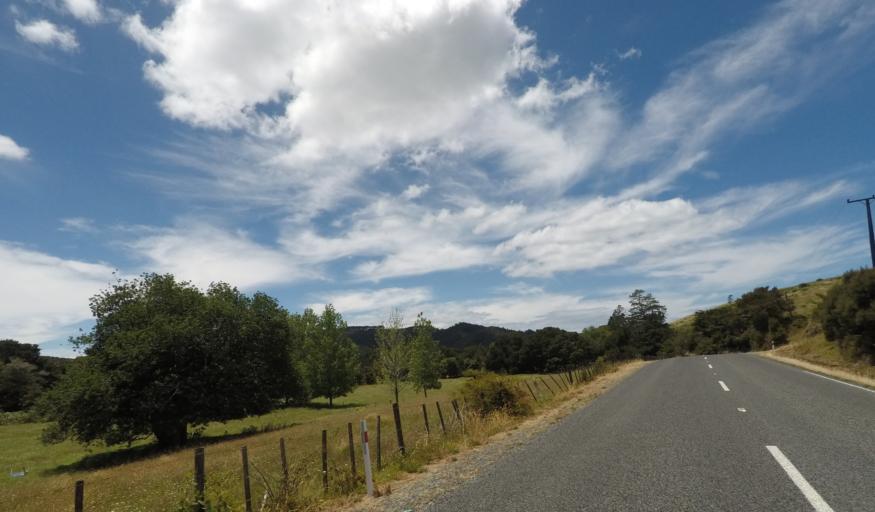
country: NZ
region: Northland
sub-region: Whangarei
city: Ngunguru
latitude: -35.5069
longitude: 174.4219
